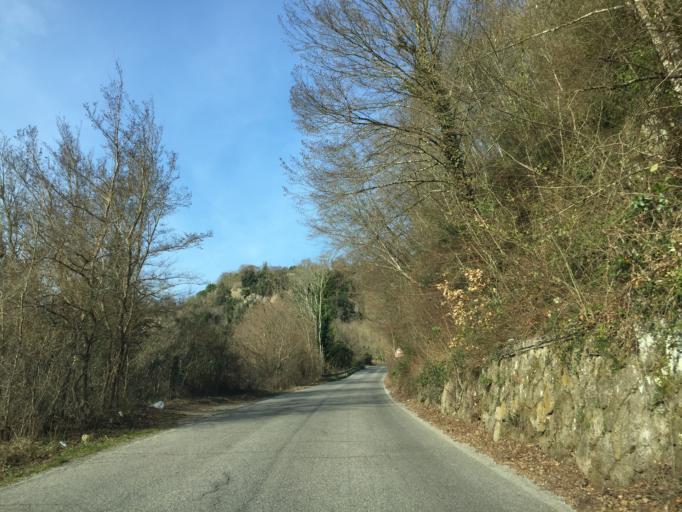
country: IT
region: Latium
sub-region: Provincia di Viterbo
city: Calcata Nuova
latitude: 42.2122
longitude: 12.4235
